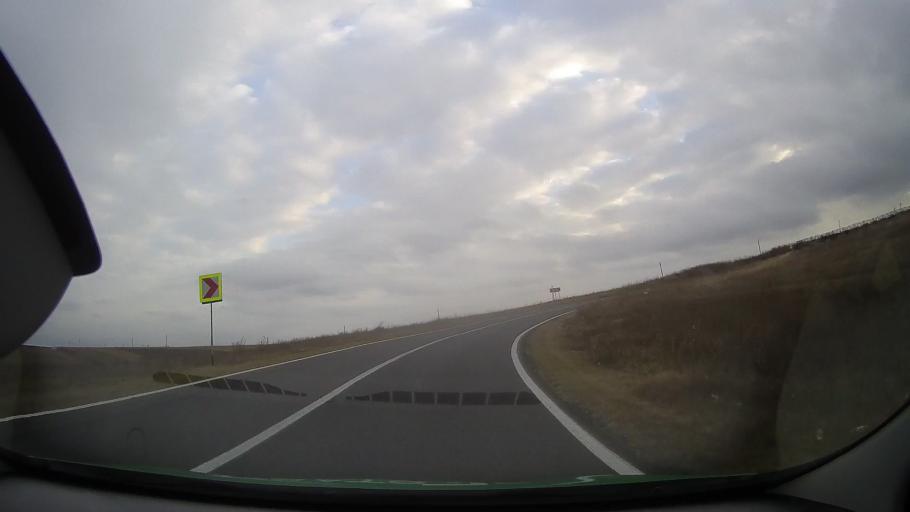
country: RO
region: Constanta
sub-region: Comuna Deleni
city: Deleni
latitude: 44.0937
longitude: 28.0173
